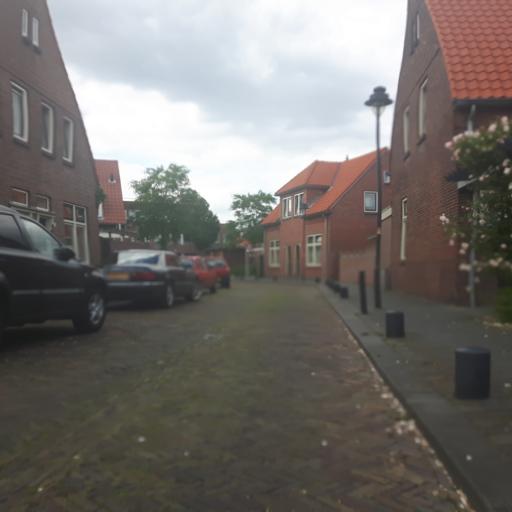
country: NL
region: Overijssel
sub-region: Gemeente Enschede
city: Enschede
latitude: 52.2144
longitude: 6.8743
